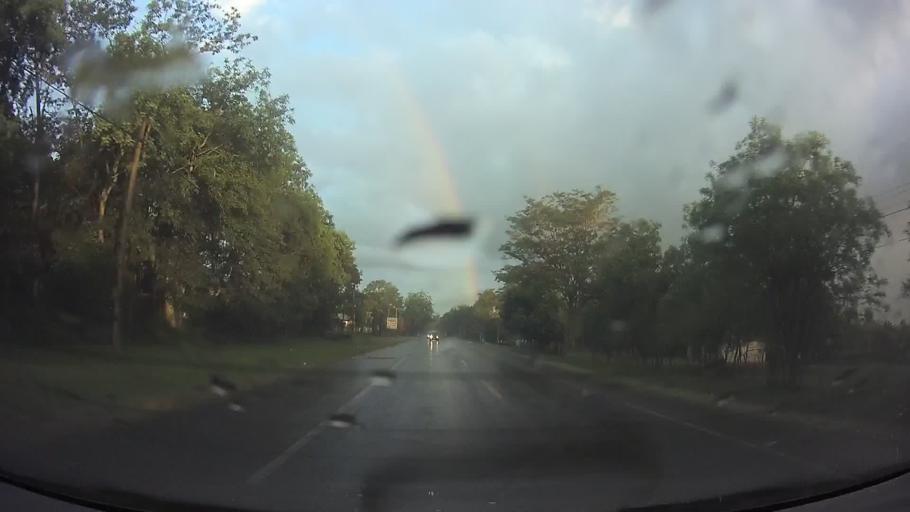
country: PY
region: Paraguari
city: Paraguari
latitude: -25.5970
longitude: -57.2103
